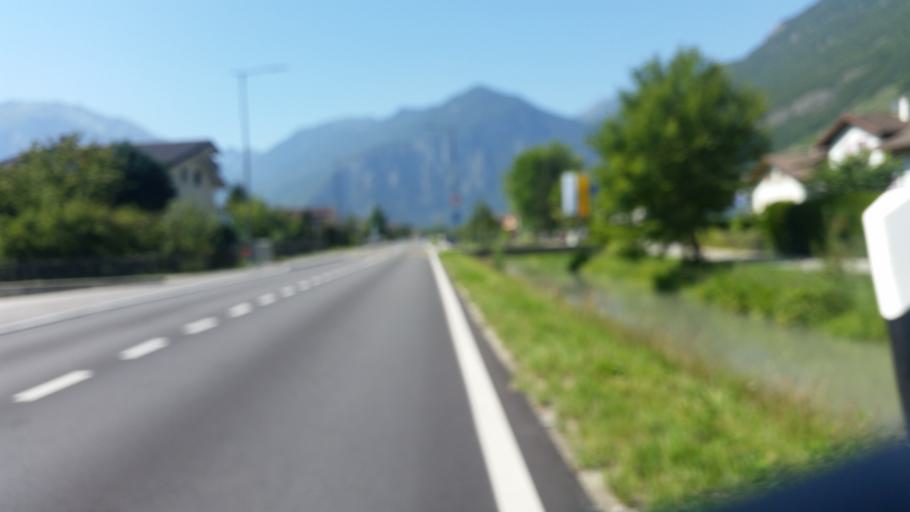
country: CH
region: Valais
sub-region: Martigny District
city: Fully
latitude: 46.1341
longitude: 7.1114
